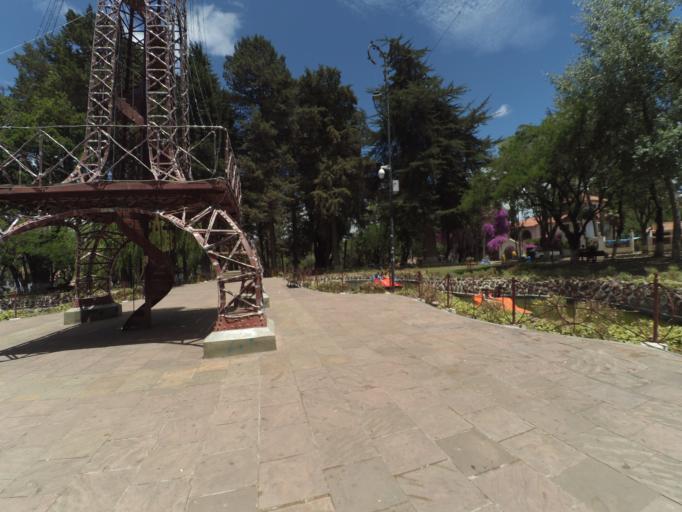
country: BO
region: Chuquisaca
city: Sucre
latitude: -19.0419
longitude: -65.2641
